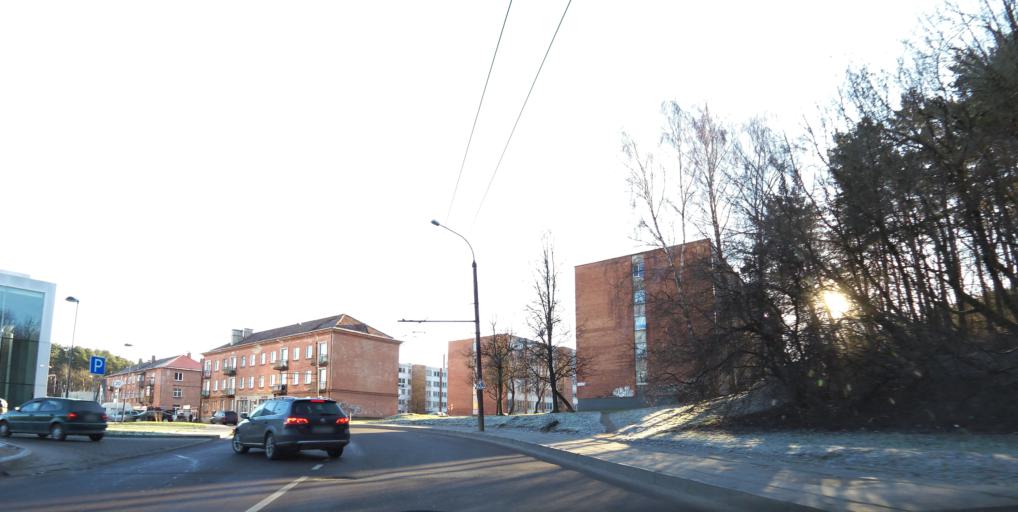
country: LT
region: Vilnius County
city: Lazdynai
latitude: 54.6430
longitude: 25.2025
